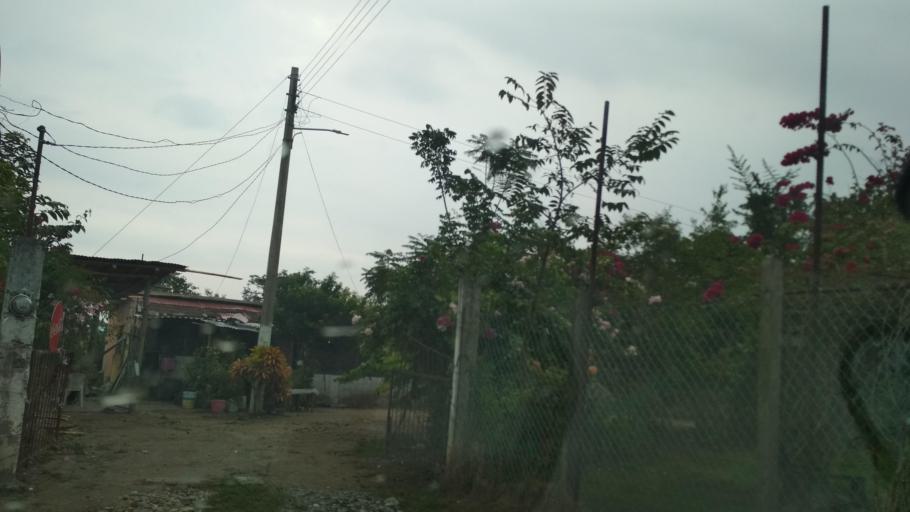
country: MM
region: Shan
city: Taunggyi
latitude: 20.3354
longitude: 97.3086
